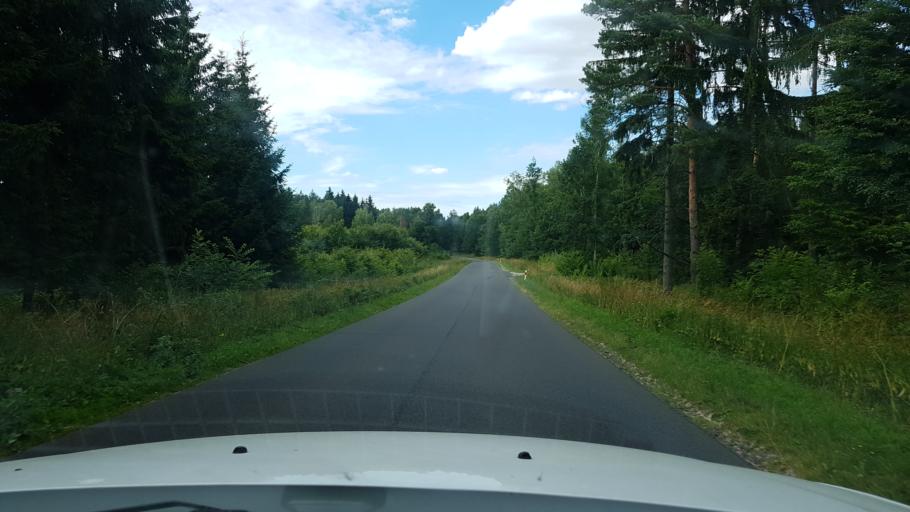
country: PL
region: West Pomeranian Voivodeship
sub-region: Powiat drawski
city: Zlocieniec
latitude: 53.5001
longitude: 16.0287
